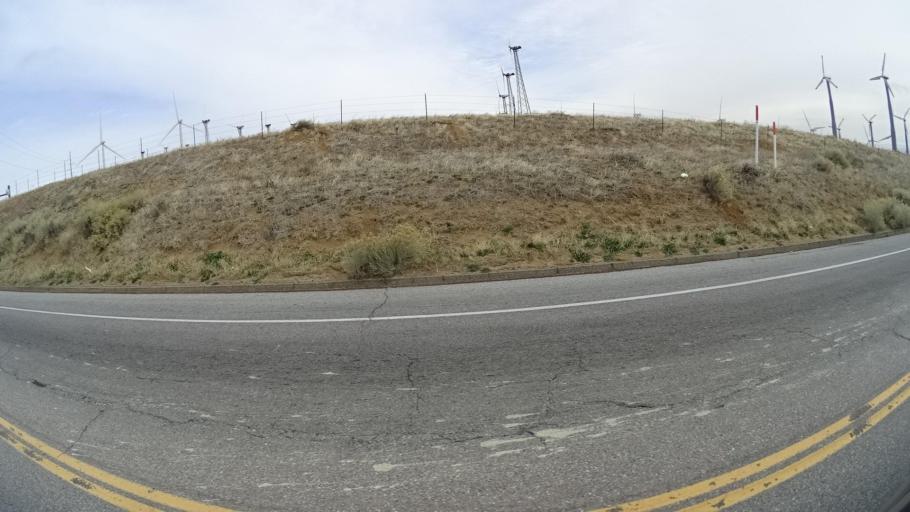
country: US
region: California
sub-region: Kern County
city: Tehachapi
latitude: 35.0596
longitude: -118.3869
